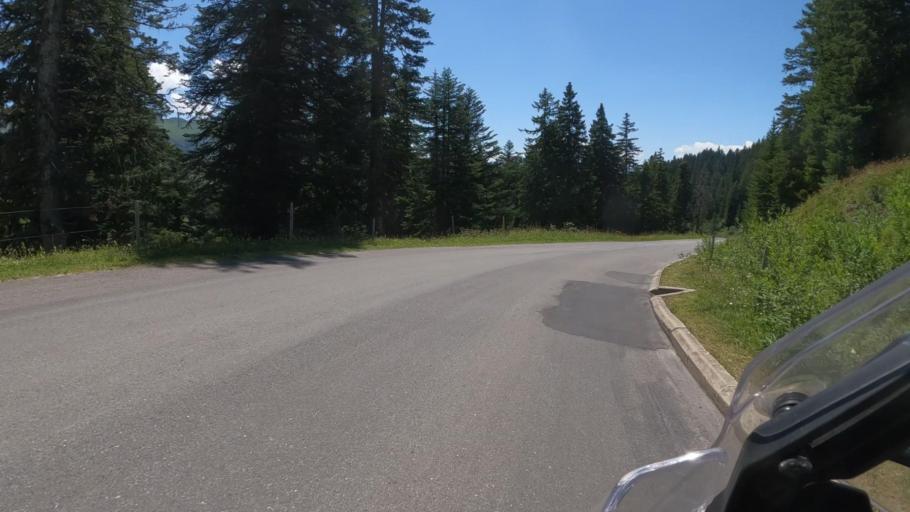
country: CH
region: Vaud
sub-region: Aigle District
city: Villars-sur-Ollon
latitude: 46.3215
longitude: 7.1219
